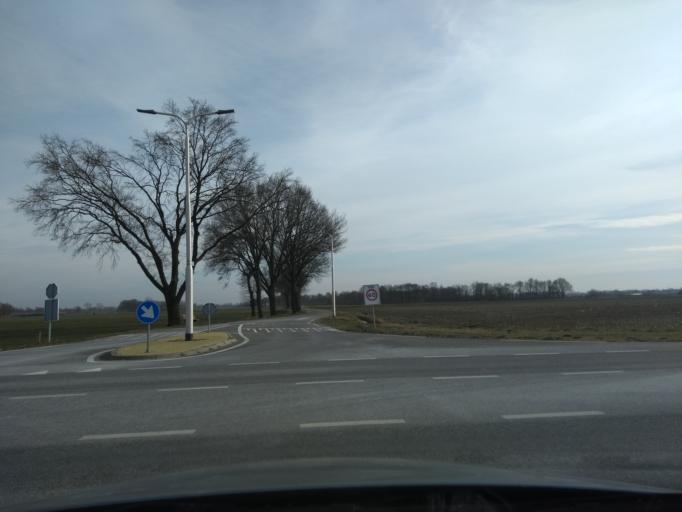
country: NL
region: Overijssel
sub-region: Gemeente Twenterand
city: Vriezenveen
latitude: 52.4183
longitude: 6.6577
